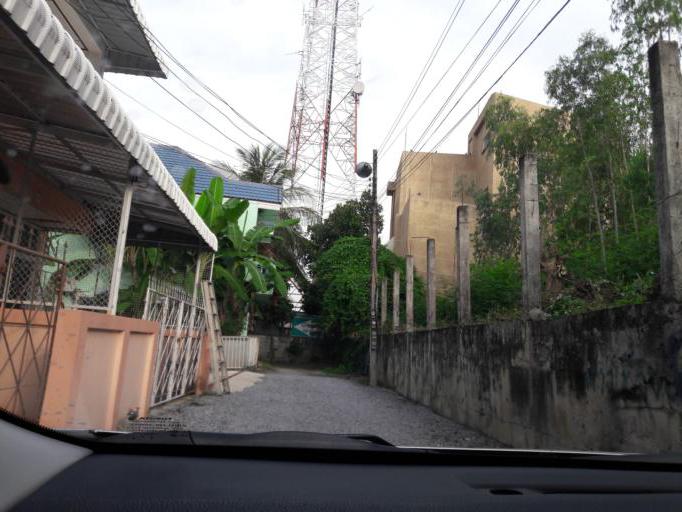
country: TH
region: Ang Thong
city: Ang Thong
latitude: 14.5864
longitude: 100.4566
